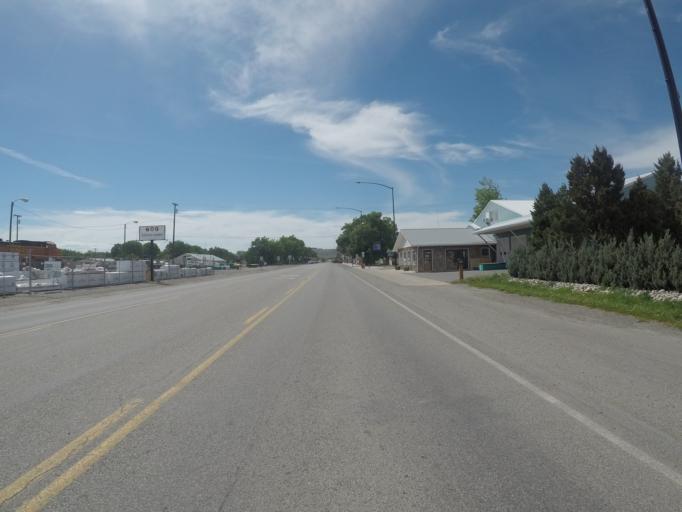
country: US
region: Montana
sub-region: Stillwater County
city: Columbus
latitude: 45.6364
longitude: -109.2502
